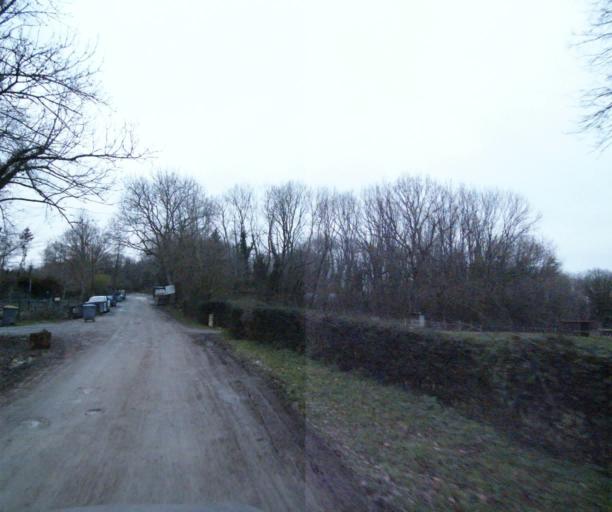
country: FR
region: Ile-de-France
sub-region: Departement de Seine-et-Marne
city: Longperrier
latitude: 49.0639
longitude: 2.6559
